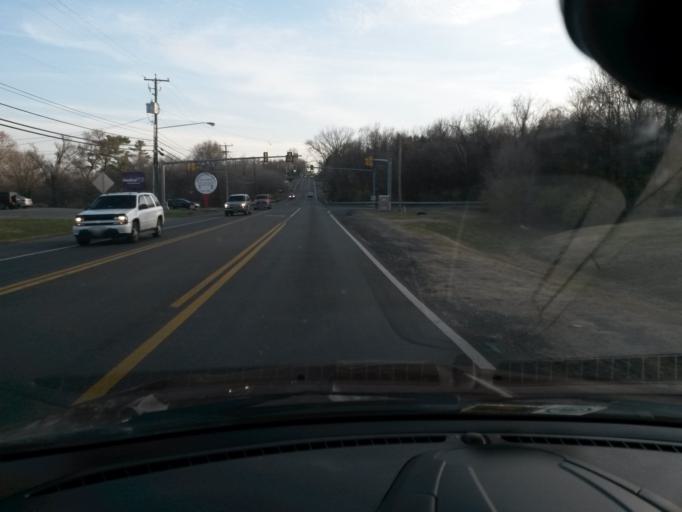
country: US
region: Virginia
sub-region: Roanoke County
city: Hollins
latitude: 37.3349
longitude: -79.9551
